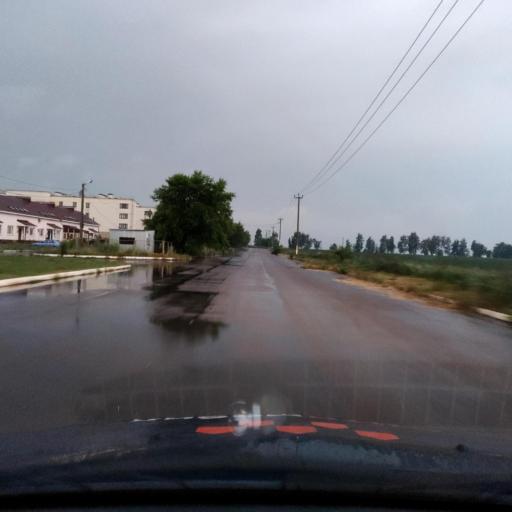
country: RU
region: Voronezj
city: Novaya Usman'
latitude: 51.6188
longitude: 39.3276
